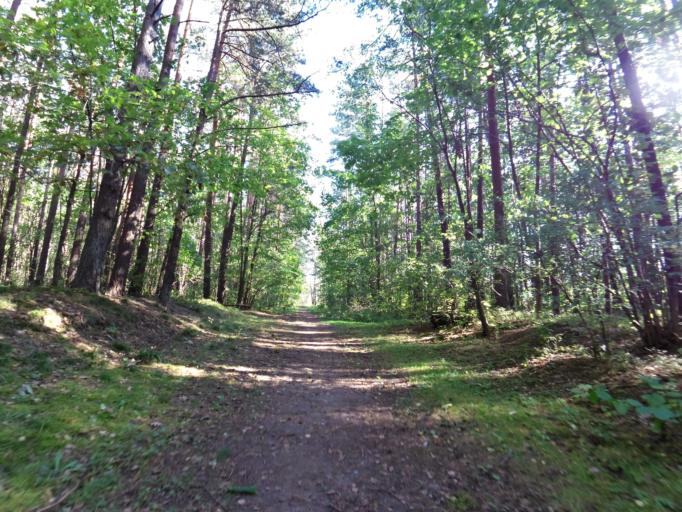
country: LT
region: Vilnius County
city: Pilaite
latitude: 54.6884
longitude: 25.1945
